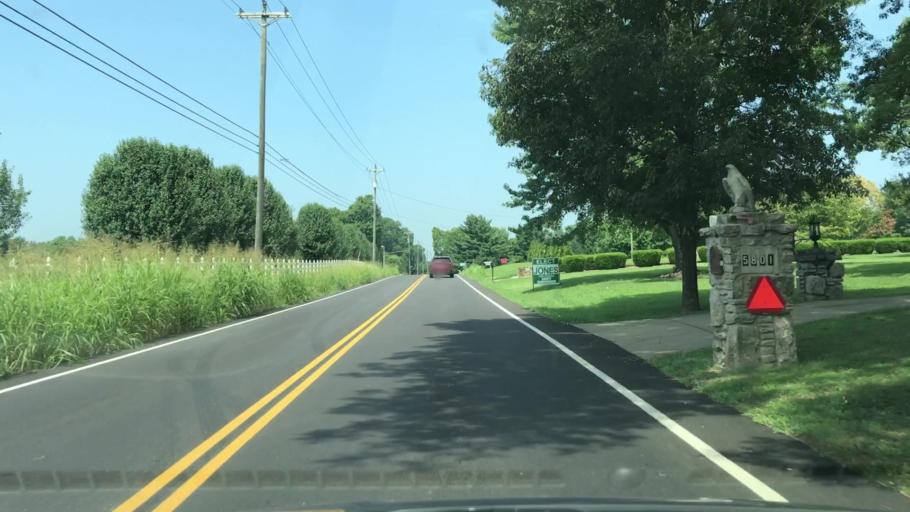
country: US
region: Tennessee
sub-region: Wilson County
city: Rural Hill
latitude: 36.1164
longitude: -86.4714
